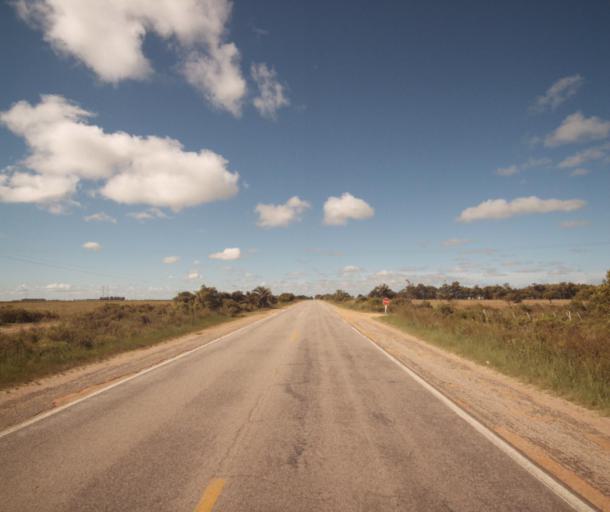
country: BR
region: Rio Grande do Sul
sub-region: Santa Vitoria Do Palmar
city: Santa Vitoria do Palmar
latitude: -33.3783
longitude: -53.1951
